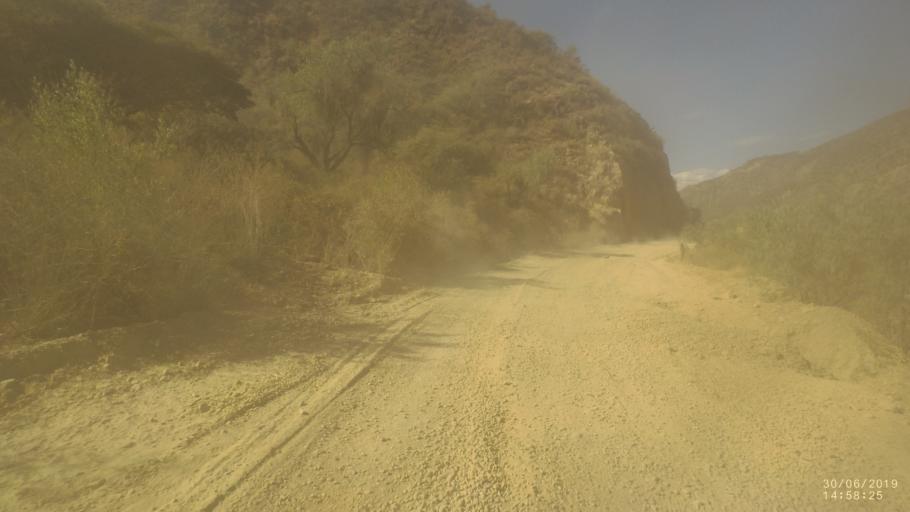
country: BO
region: Cochabamba
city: Irpa Irpa
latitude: -17.7386
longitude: -66.3495
